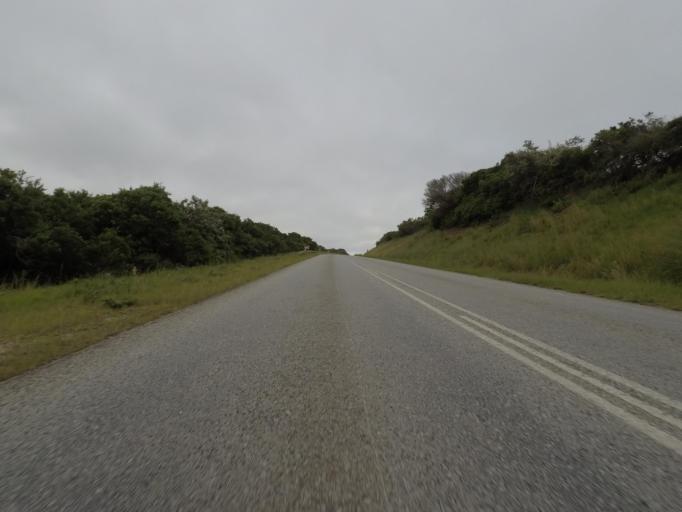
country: ZA
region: Eastern Cape
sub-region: Cacadu District Municipality
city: Port Alfred
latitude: -33.6118
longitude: 26.8064
